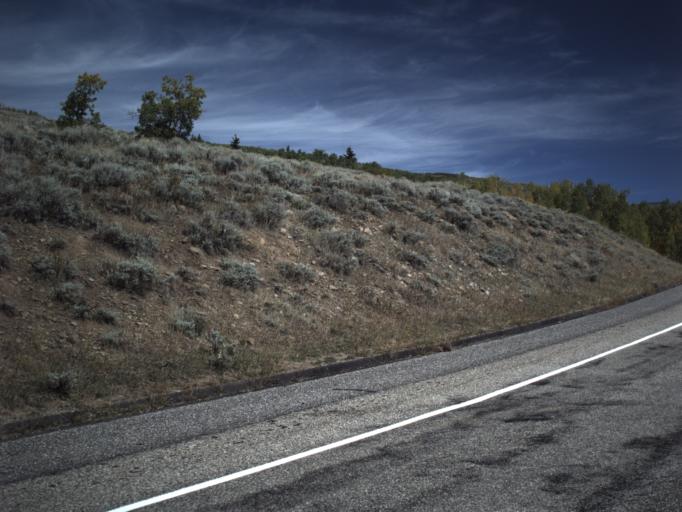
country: US
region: Utah
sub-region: Wayne County
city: Loa
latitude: 38.0096
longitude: -111.3832
